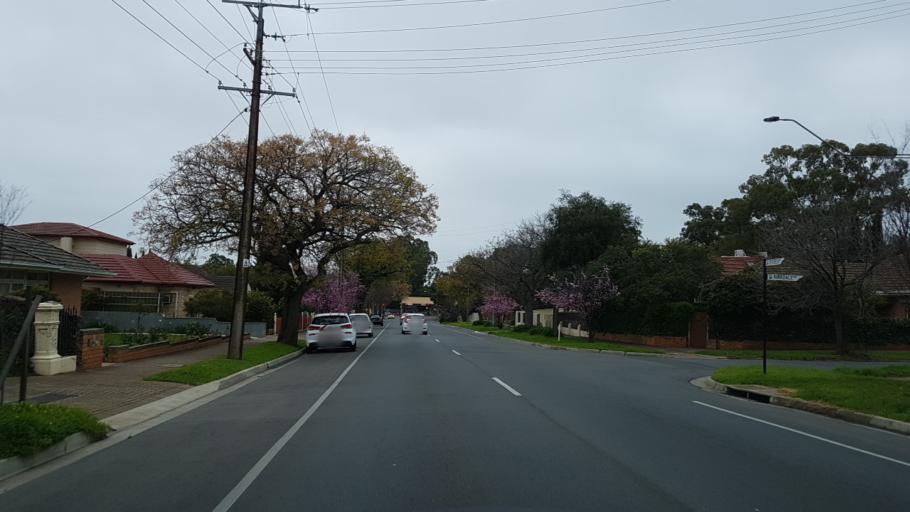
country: AU
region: South Australia
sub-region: Burnside
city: Tusmore
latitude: -34.9408
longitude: 138.6515
